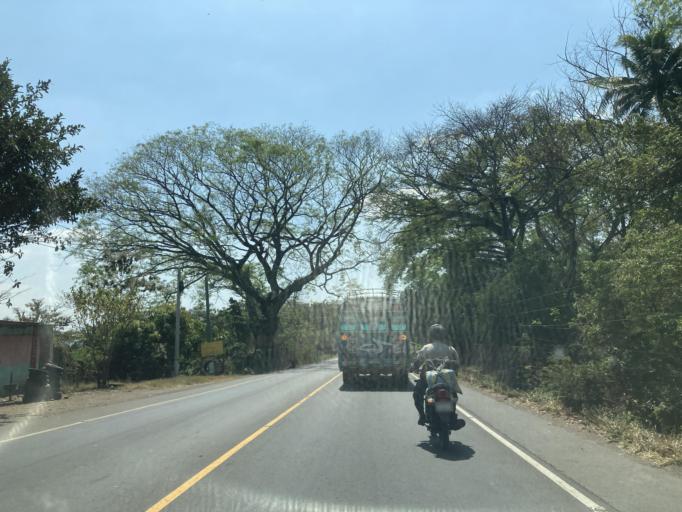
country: GT
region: Escuintla
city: Guanagazapa
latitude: 14.2171
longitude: -90.7254
